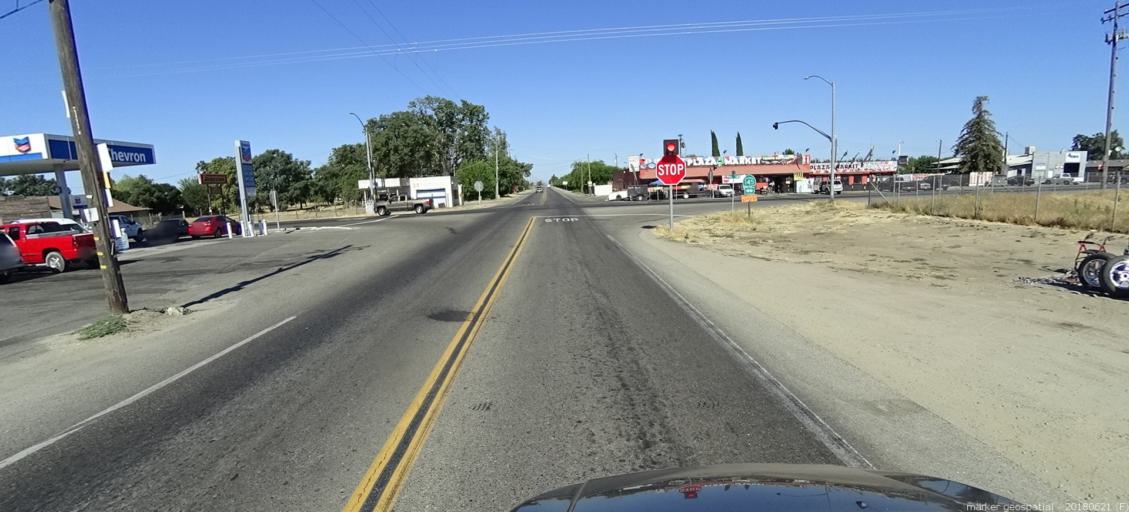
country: US
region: California
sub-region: Fresno County
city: Biola
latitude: 36.8514
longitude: -120.0553
